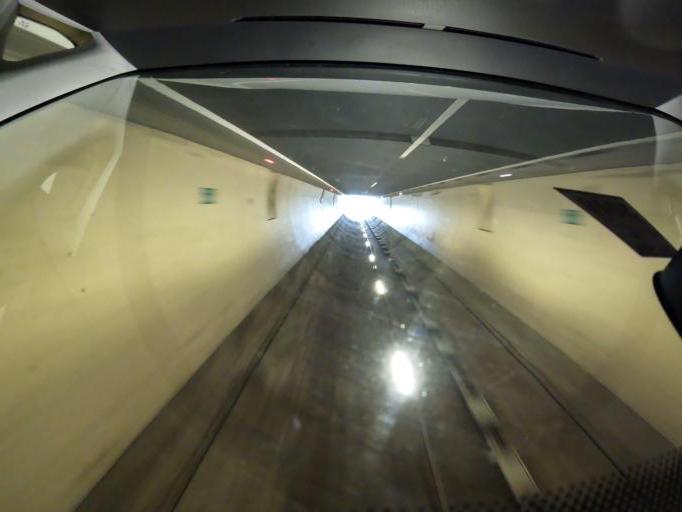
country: AT
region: Carinthia
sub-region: Politischer Bezirk Volkermarkt
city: Ruden
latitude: 46.7043
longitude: 14.7809
